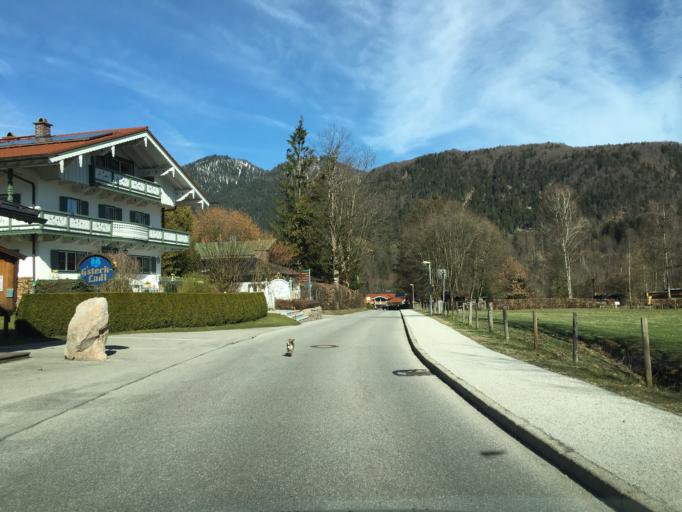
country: DE
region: Bavaria
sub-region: Upper Bavaria
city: Schoenau am Koenigssee
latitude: 47.6109
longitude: 12.9595
